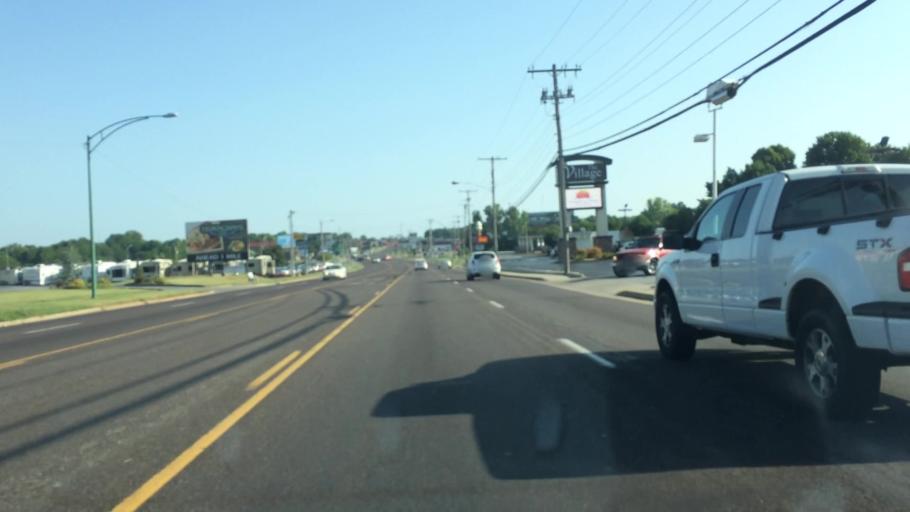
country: US
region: Missouri
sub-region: Greene County
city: Springfield
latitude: 37.1633
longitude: -93.2953
